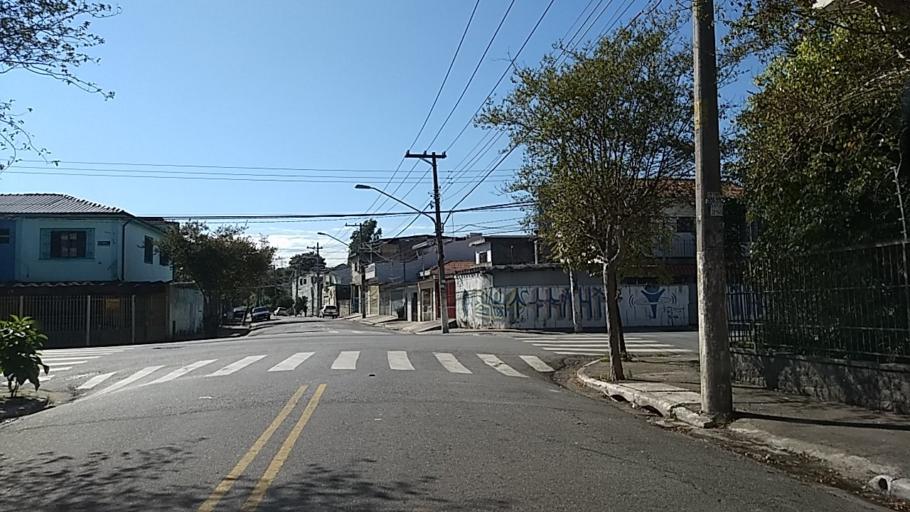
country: BR
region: Sao Paulo
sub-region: Guarulhos
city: Guarulhos
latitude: -23.4801
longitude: -46.5631
